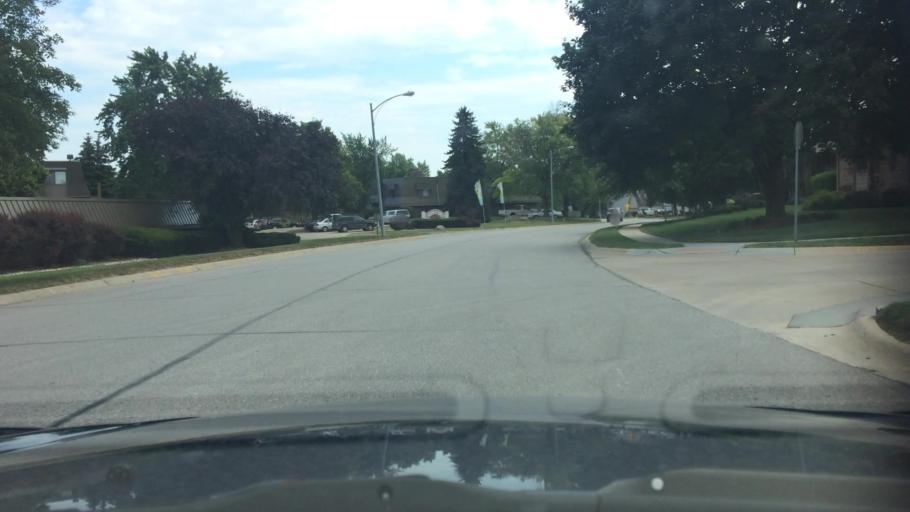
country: US
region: Nebraska
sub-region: Douglas County
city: Ralston
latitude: 41.1965
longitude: -96.0682
